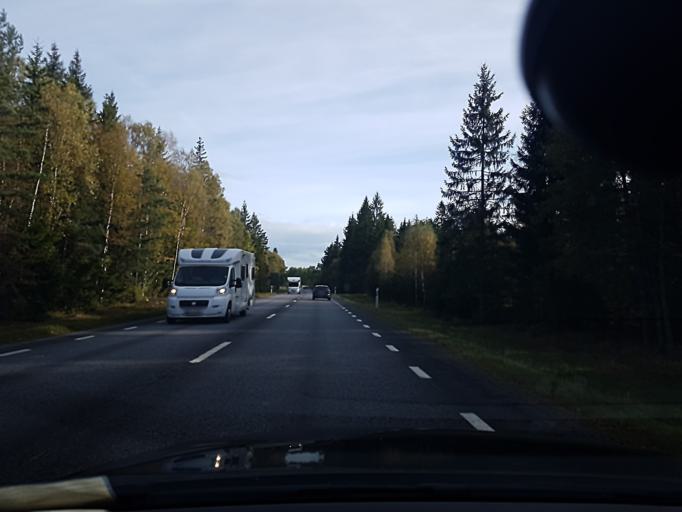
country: SE
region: Joenkoeping
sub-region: Varnamo Kommun
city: Varnamo
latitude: 57.1469
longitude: 14.0962
